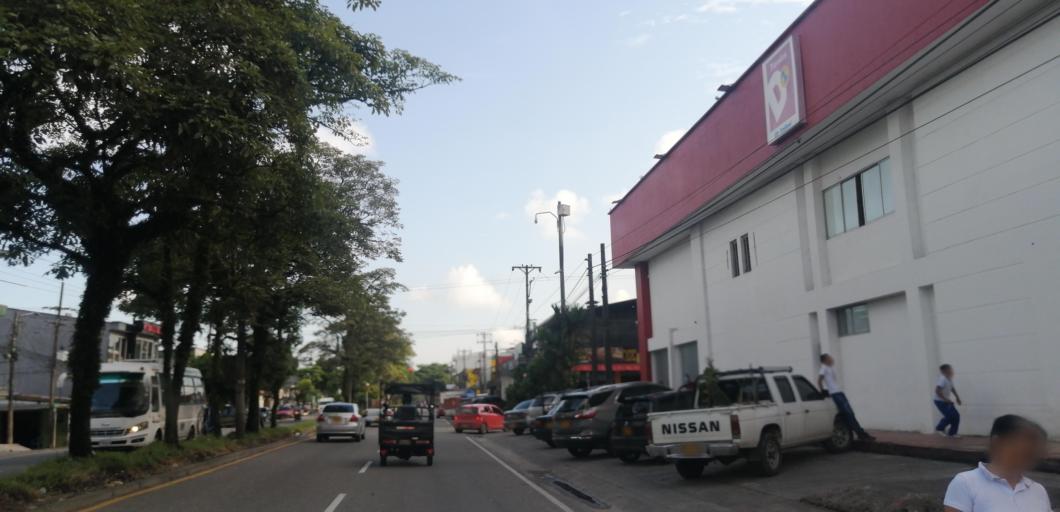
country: CO
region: Meta
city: Acacias
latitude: 3.9859
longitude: -73.7663
